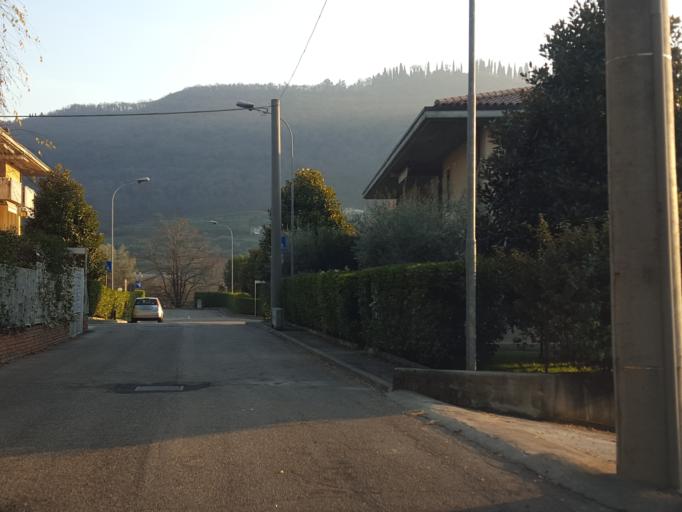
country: IT
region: Veneto
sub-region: Provincia di Verona
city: Garda
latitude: 45.5788
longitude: 10.7185
